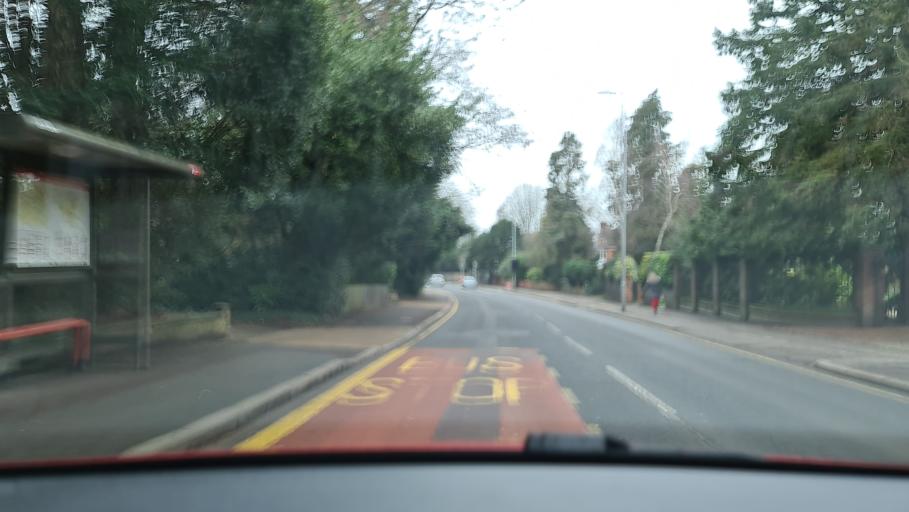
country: GB
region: England
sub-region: Greater London
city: Surbiton
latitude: 51.3883
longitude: -0.3035
